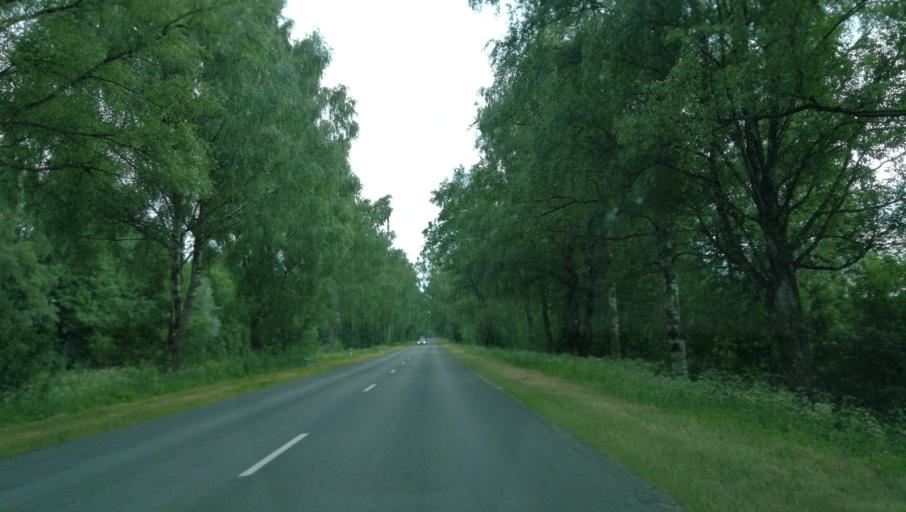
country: LV
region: Valmieras Rajons
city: Valmiera
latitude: 57.6666
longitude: 25.4294
